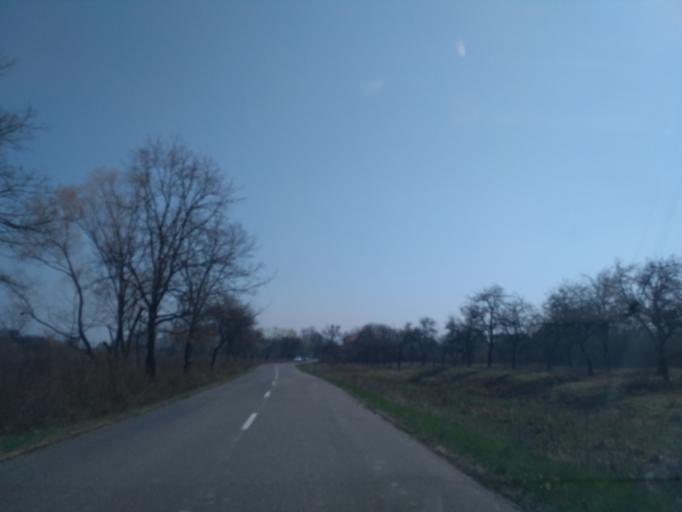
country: SK
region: Kosicky
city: Secovce
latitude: 48.7368
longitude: 21.6088
